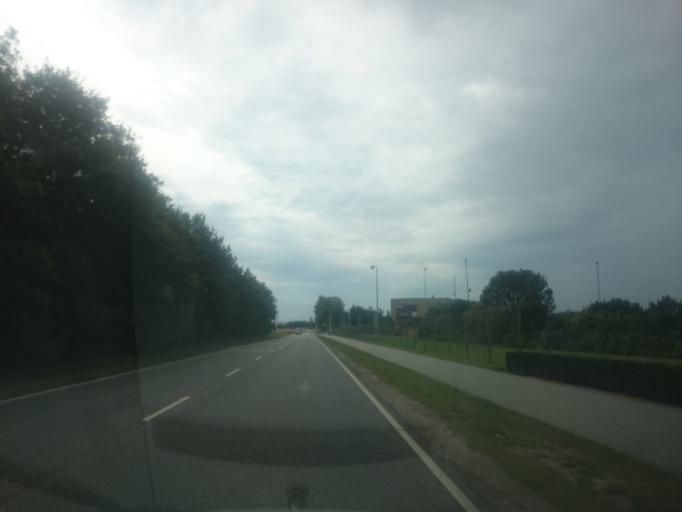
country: DK
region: South Denmark
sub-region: Billund Kommune
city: Billund
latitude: 55.7305
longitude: 9.1330
